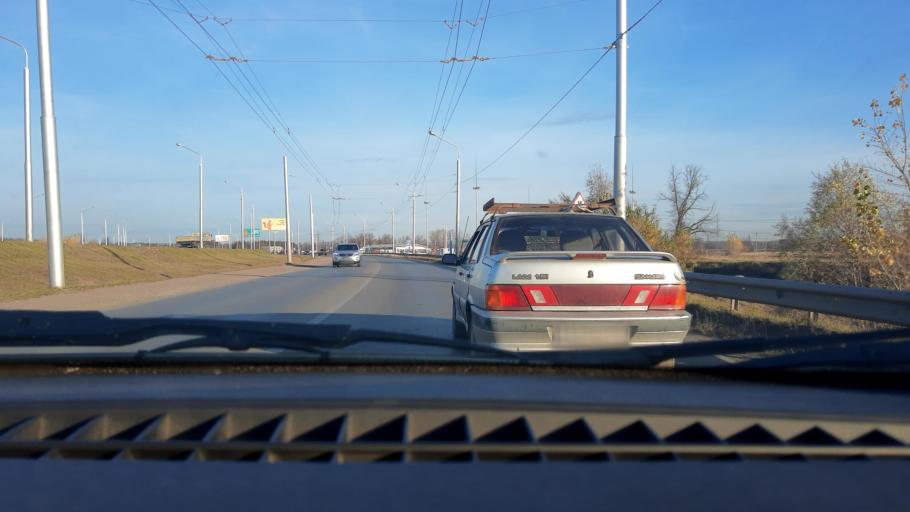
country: RU
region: Bashkortostan
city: Ufa
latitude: 54.7722
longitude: 55.9544
